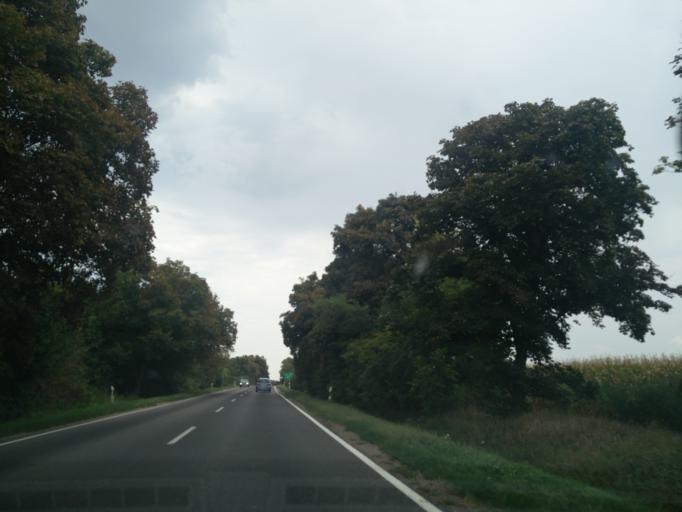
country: HU
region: Fejer
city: Polgardi
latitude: 47.0628
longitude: 18.3087
